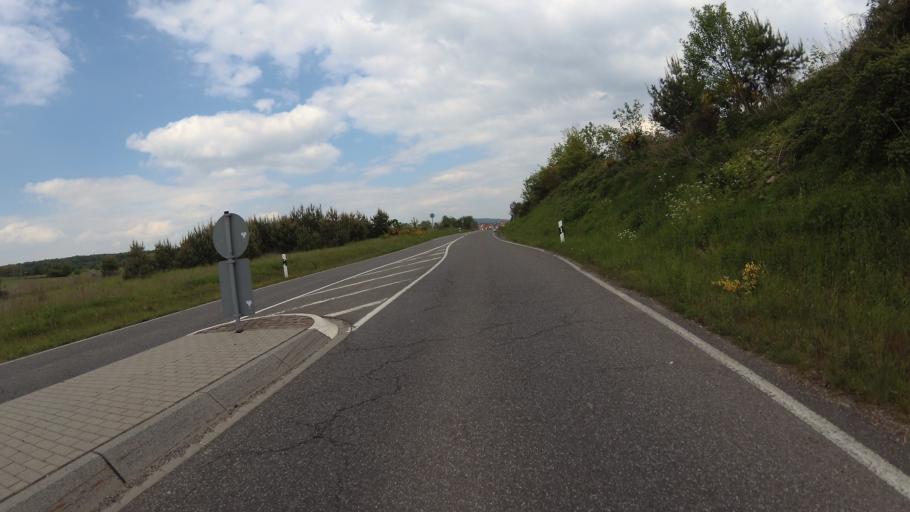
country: DE
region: Rheinland-Pfalz
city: Mackenbach
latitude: 49.4721
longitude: 7.5749
